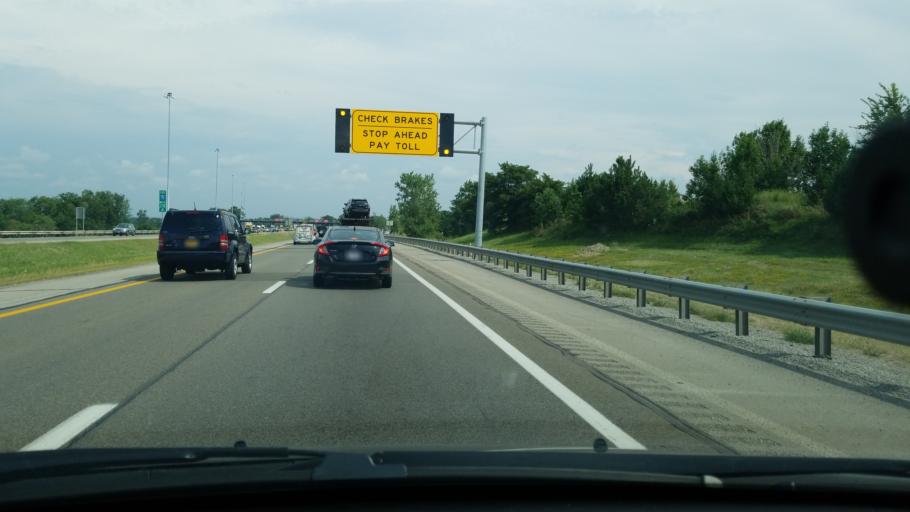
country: US
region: Ohio
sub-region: Mahoning County
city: New Middletown
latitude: 40.9264
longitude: -80.5615
